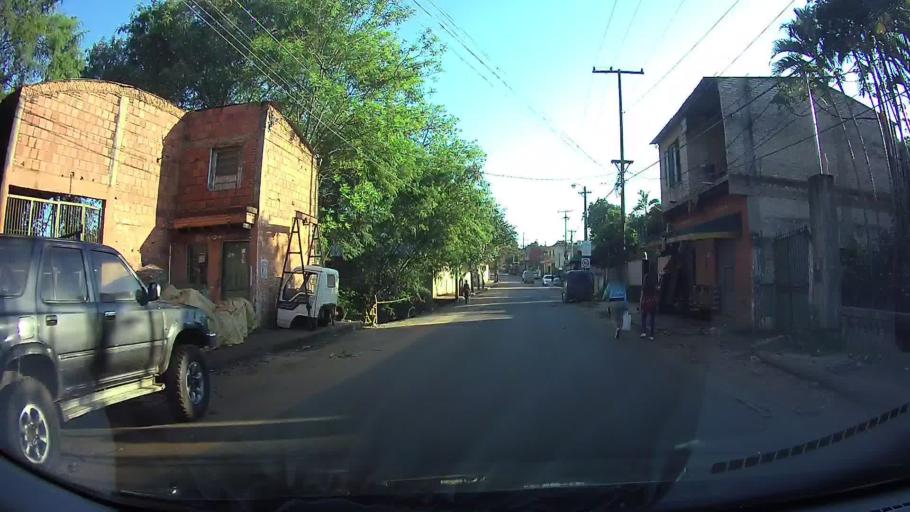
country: PY
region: Central
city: Fernando de la Mora
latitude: -25.3379
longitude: -57.5298
